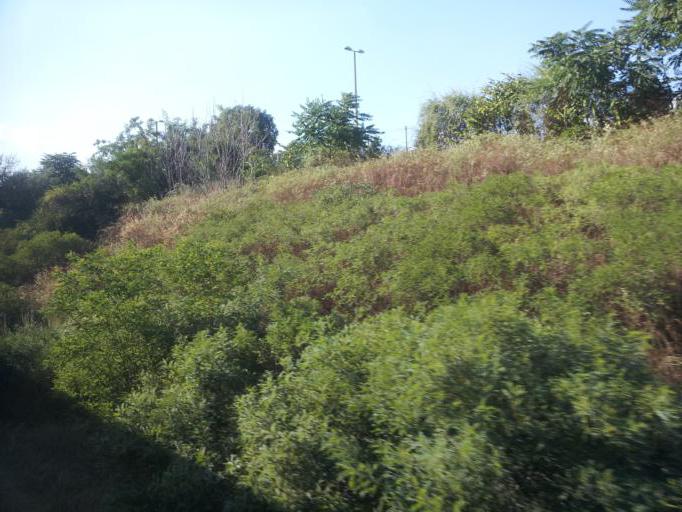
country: HU
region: Budapest
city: Budapest XXIII. keruelet
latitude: 47.4147
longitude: 19.1120
